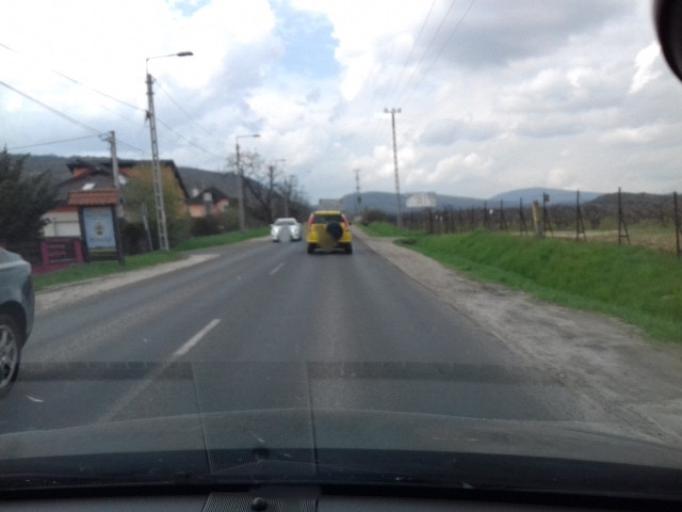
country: HU
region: Pest
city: Nagykovacsi
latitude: 47.6515
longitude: 18.9950
